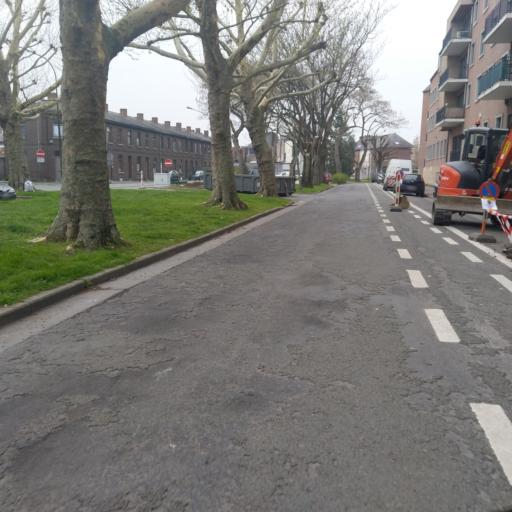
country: BE
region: Wallonia
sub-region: Province du Hainaut
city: Mons
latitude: 50.4473
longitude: 3.9555
